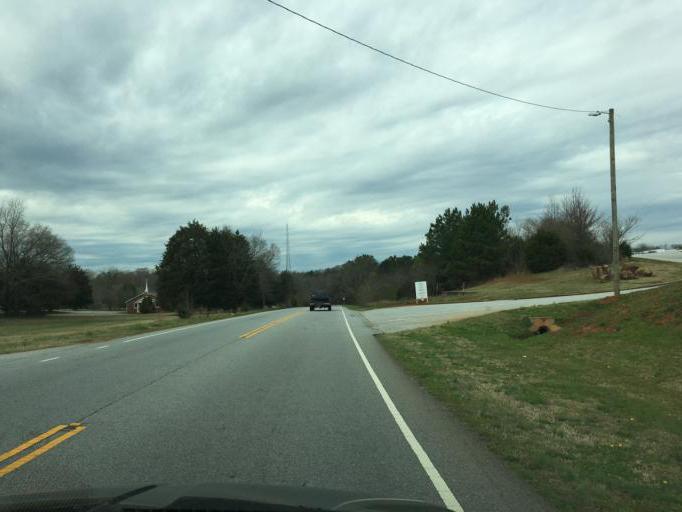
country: US
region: South Carolina
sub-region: Anderson County
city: Piedmont
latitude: 34.7065
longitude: -82.4449
